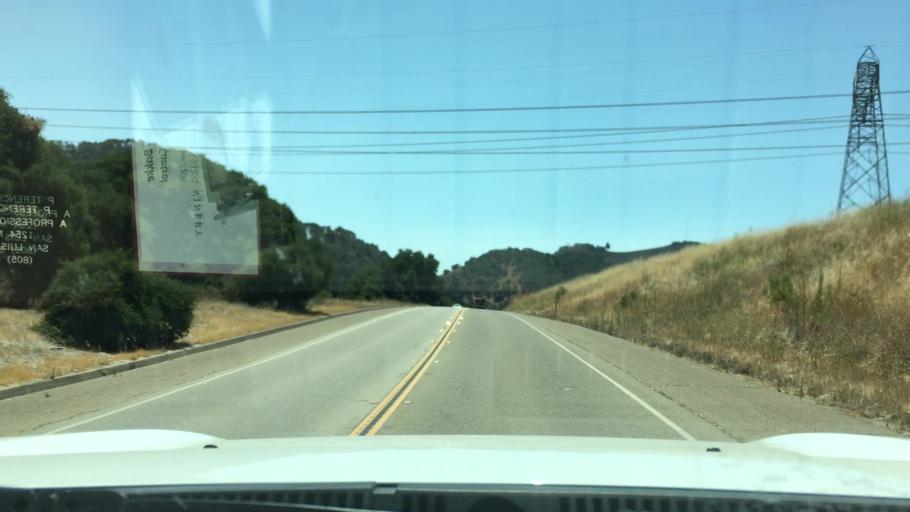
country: US
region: California
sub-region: San Luis Obispo County
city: Pismo Beach
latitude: 35.1723
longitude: -120.6241
